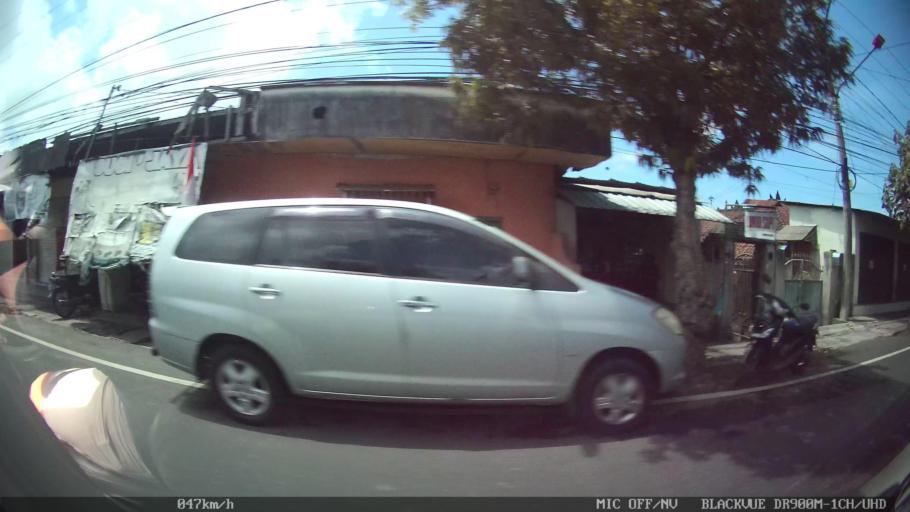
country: ID
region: Bali
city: Banjar Desa
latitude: -8.5895
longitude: 115.2825
